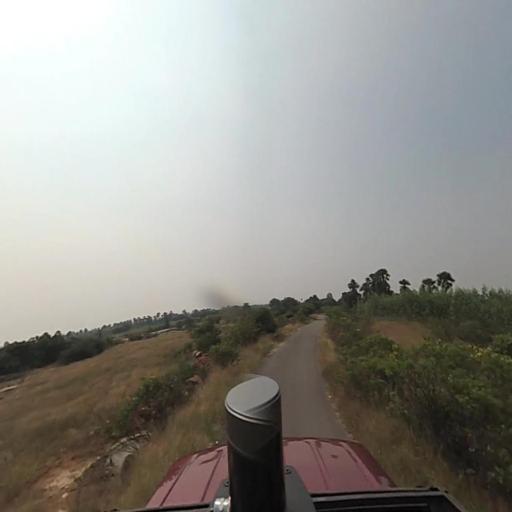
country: IN
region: Telangana
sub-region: Nalgonda
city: Nalgonda
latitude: 17.1999
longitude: 79.1425
